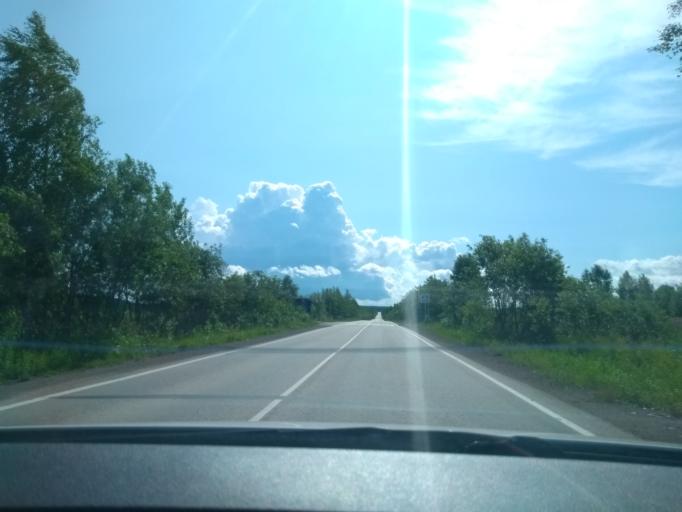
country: RU
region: Perm
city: Bershet'
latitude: 57.8215
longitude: 56.4316
